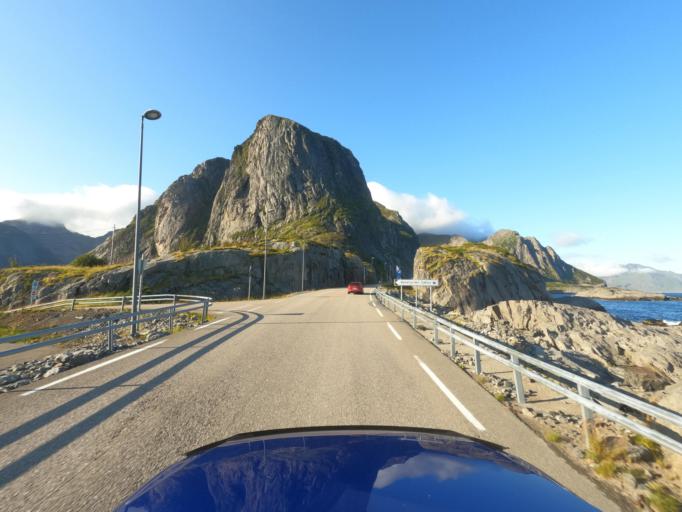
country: NO
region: Nordland
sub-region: Moskenes
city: Reine
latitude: 67.9482
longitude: 13.1371
